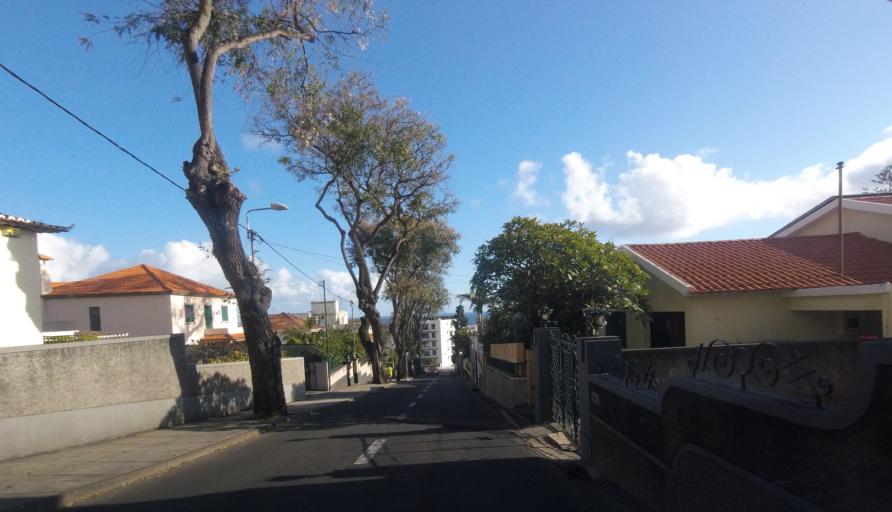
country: PT
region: Madeira
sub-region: Funchal
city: Nossa Senhora do Monte
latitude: 32.6549
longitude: -16.9049
